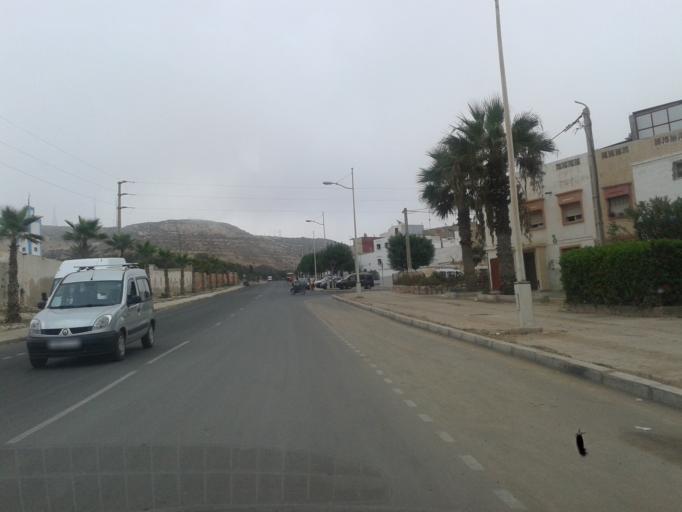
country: MA
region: Souss-Massa-Draa
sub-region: Agadir-Ida-ou-Tnan
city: Aourir
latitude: 30.4494
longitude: -9.6598
